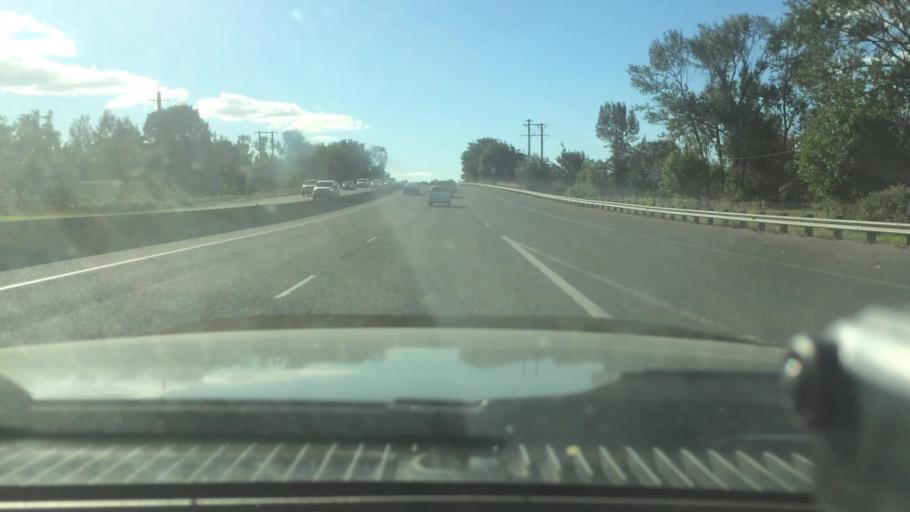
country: US
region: Oregon
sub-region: Lane County
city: Eugene
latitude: 44.0937
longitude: -123.1033
